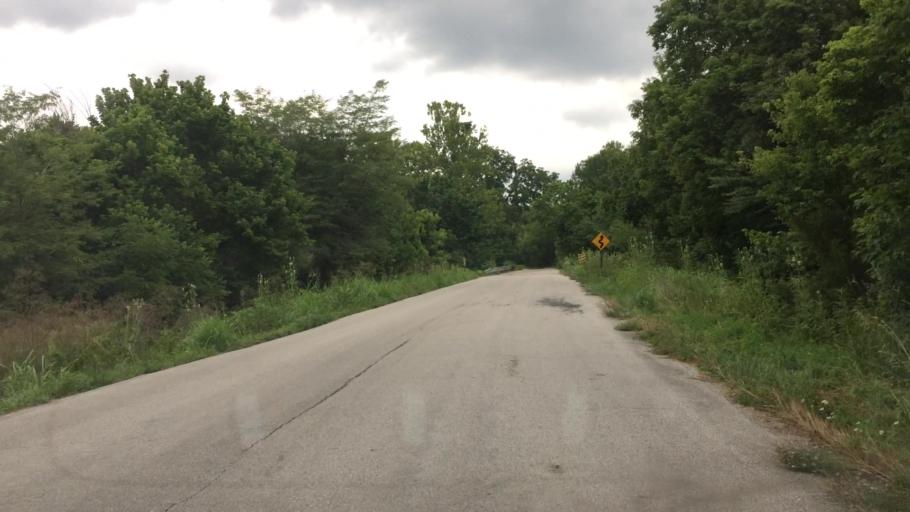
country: US
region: Missouri
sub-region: Greene County
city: Strafford
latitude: 37.3268
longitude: -93.0563
